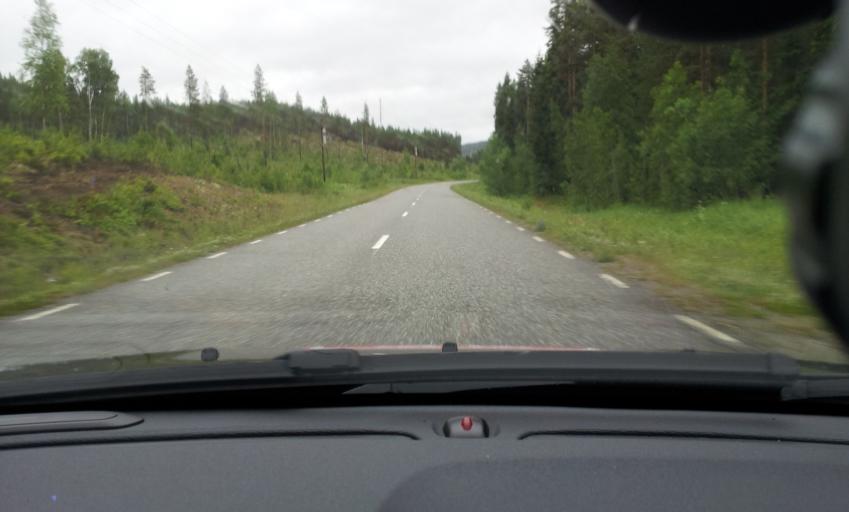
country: SE
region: Jaemtland
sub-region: Ragunda Kommun
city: Hammarstrand
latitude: 63.2746
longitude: 15.8152
